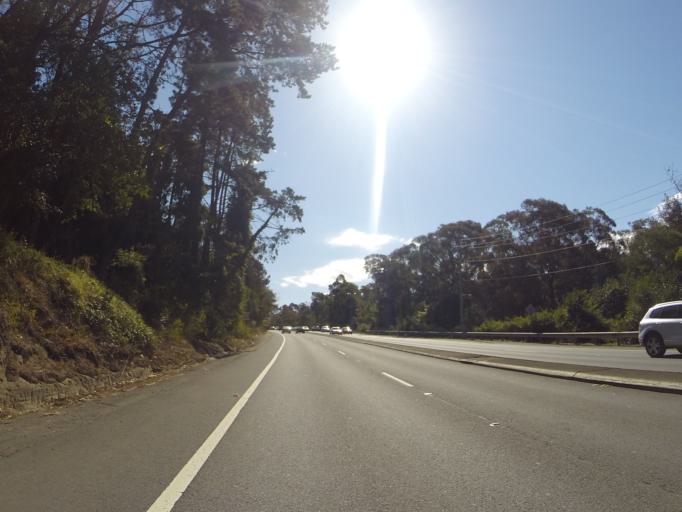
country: AU
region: New South Wales
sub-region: Blue Mountains Municipality
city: Blaxland
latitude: -33.7013
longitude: 150.5747
